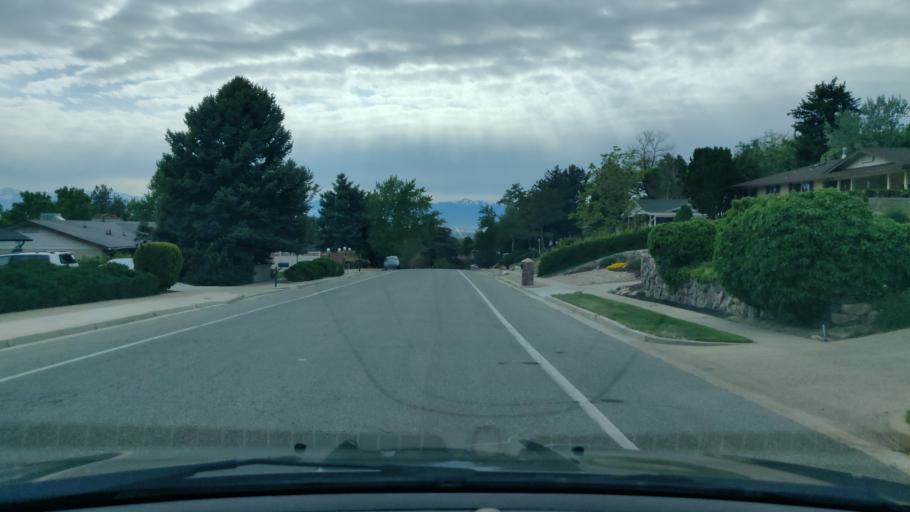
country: US
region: Utah
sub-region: Salt Lake County
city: Little Cottonwood Creek Valley
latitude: 40.6077
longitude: -111.8170
